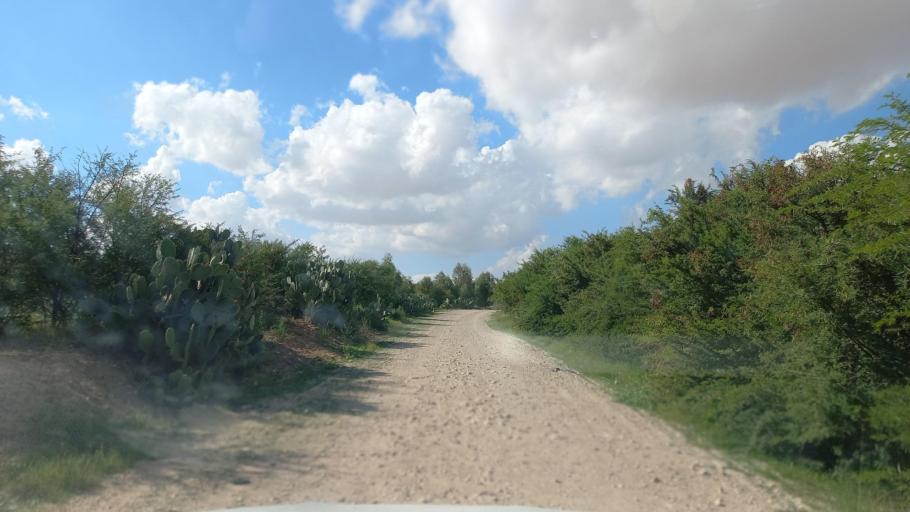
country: TN
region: Al Qasrayn
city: Sbiba
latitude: 35.3370
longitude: 9.0796
